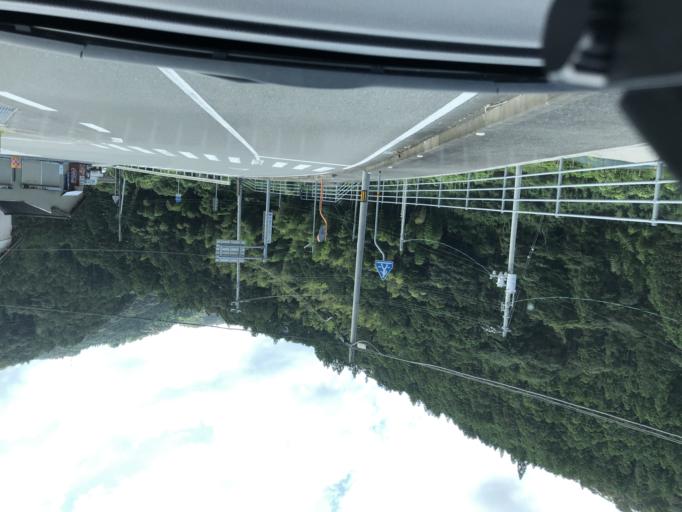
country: JP
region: Kochi
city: Kochi-shi
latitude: 33.6233
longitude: 133.4980
